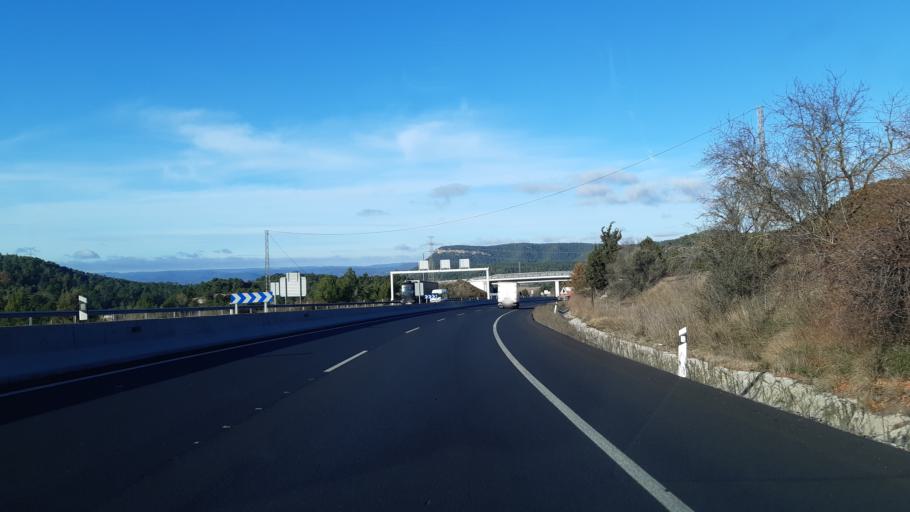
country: ES
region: Catalonia
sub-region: Provincia de Barcelona
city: Castelloli
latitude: 41.5946
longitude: 1.7229
